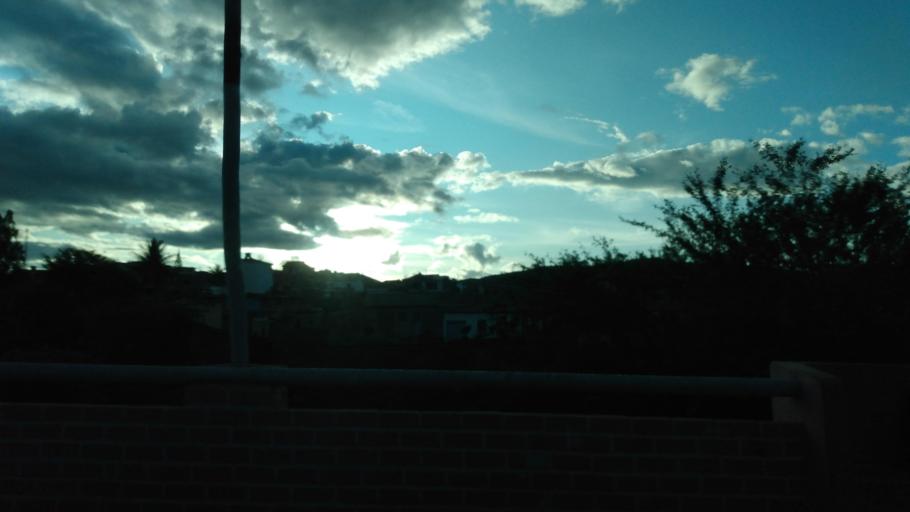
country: BR
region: Pernambuco
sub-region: Bezerros
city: Bezerros
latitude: -8.2319
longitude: -35.7504
